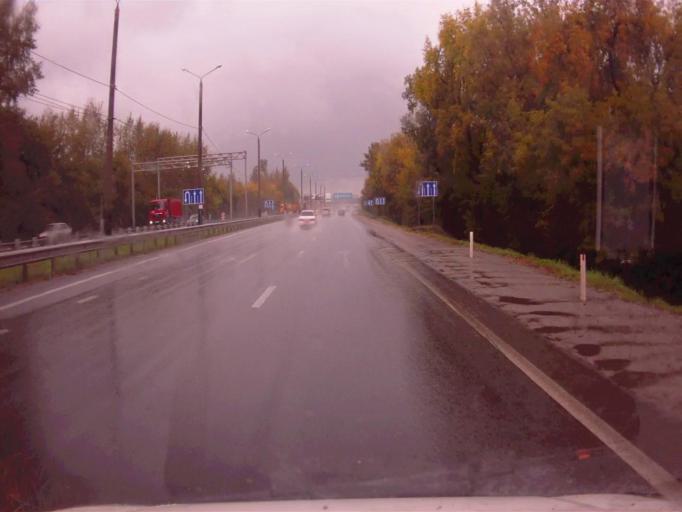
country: RU
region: Chelyabinsk
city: Dolgoderevenskoye
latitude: 55.2586
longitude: 61.3506
